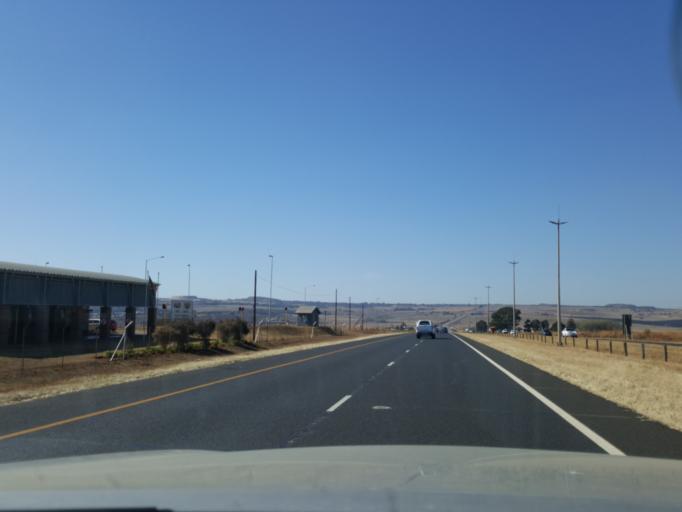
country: ZA
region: Mpumalanga
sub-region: Nkangala District Municipality
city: Middelburg
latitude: -25.8641
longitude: 29.3669
